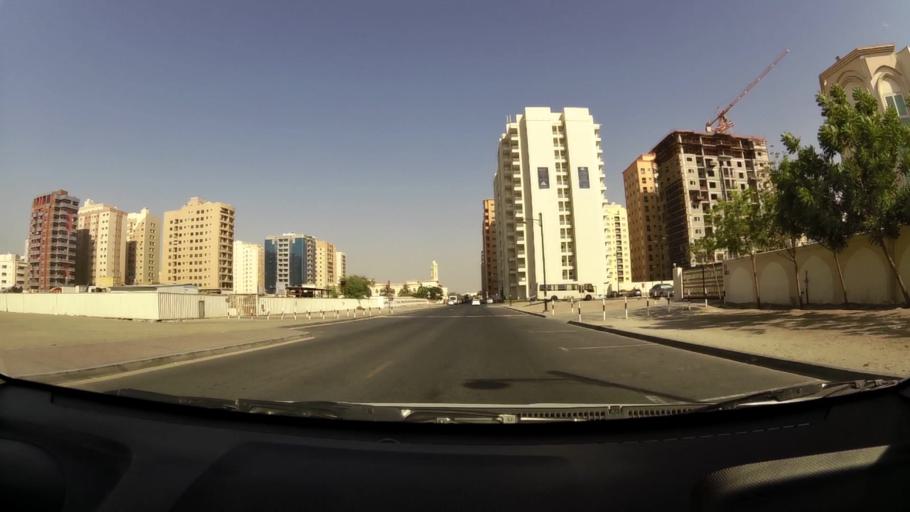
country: AE
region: Ash Shariqah
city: Sharjah
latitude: 25.2917
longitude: 55.3763
